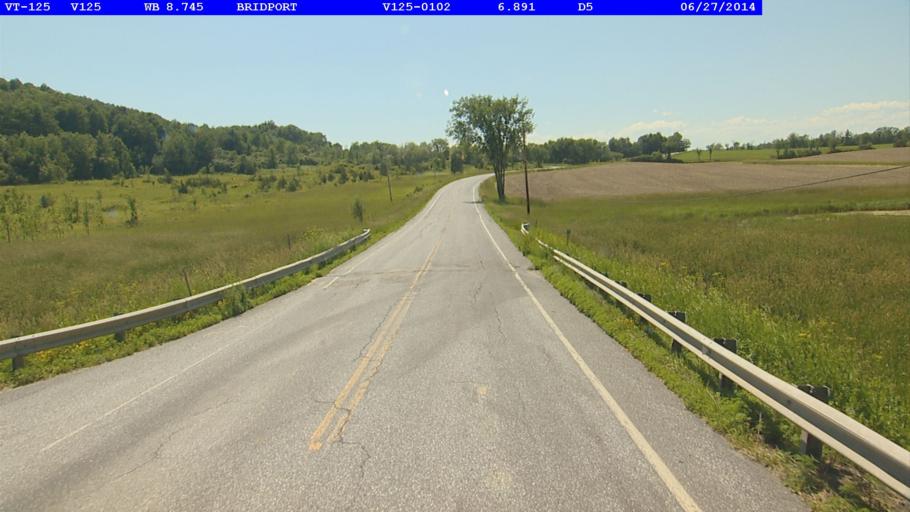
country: US
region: Vermont
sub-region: Addison County
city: Middlebury (village)
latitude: 43.9898
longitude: -73.2803
